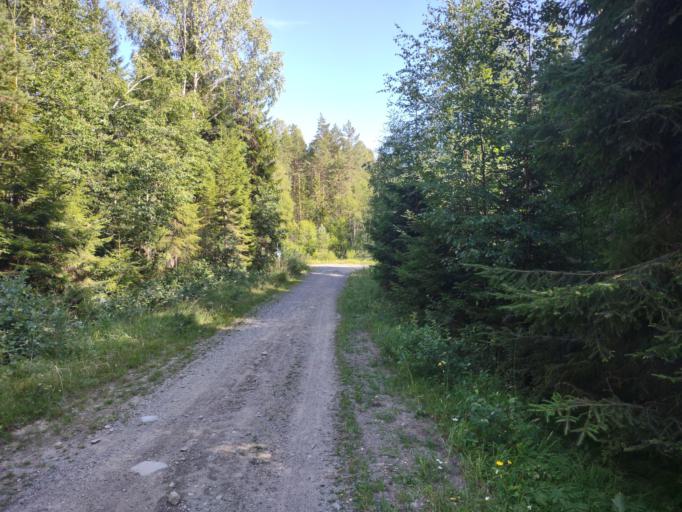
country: NO
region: Akershus
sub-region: Raelingen
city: Fjerdingby
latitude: 59.8611
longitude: 11.0165
